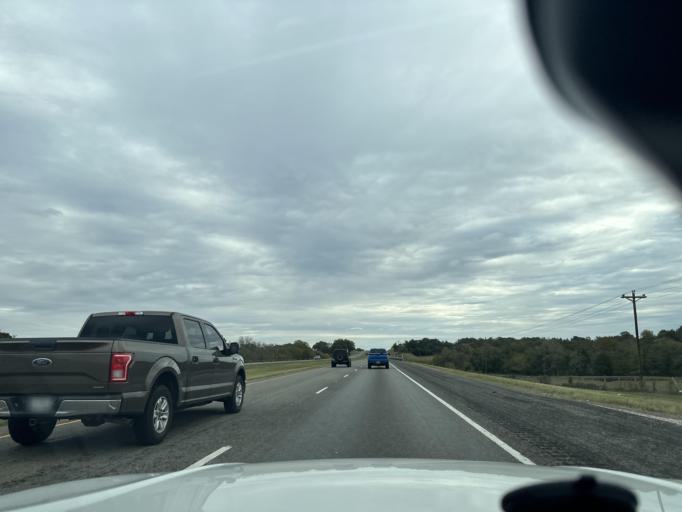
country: US
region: Texas
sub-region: Washington County
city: Brenham
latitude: 30.1878
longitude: -96.5037
